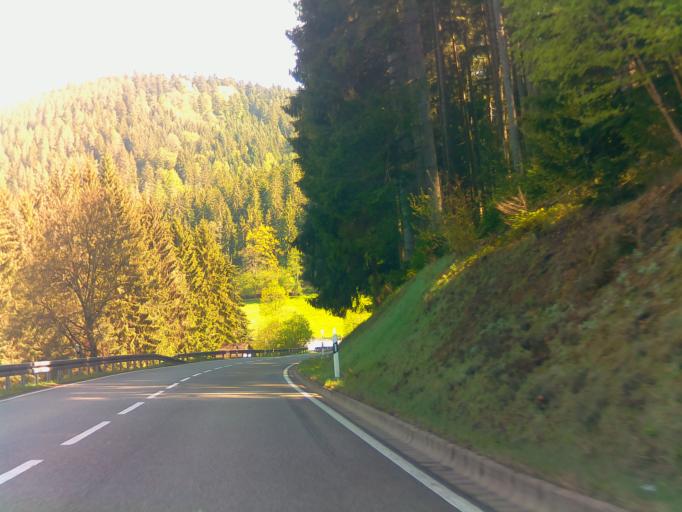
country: DE
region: Baden-Wuerttemberg
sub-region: Karlsruhe Region
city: Neuweiler
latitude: 48.6855
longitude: 8.5652
